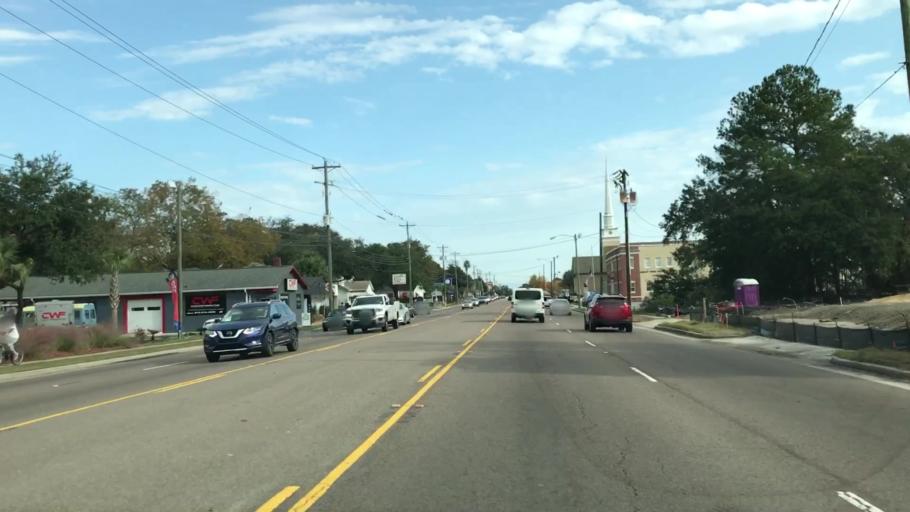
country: US
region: South Carolina
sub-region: Charleston County
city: Charleston
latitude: 32.7835
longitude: -79.9944
